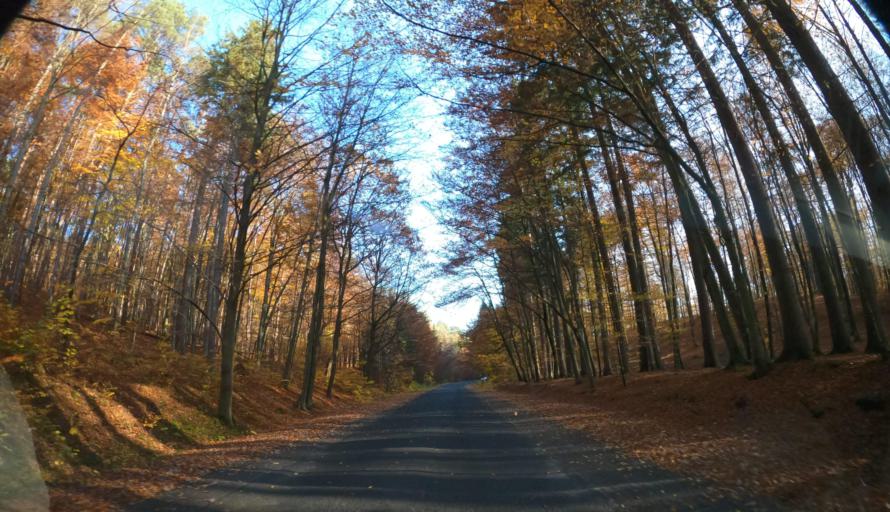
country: PL
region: West Pomeranian Voivodeship
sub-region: Powiat koszalinski
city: Polanow
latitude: 54.2397
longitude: 16.7302
